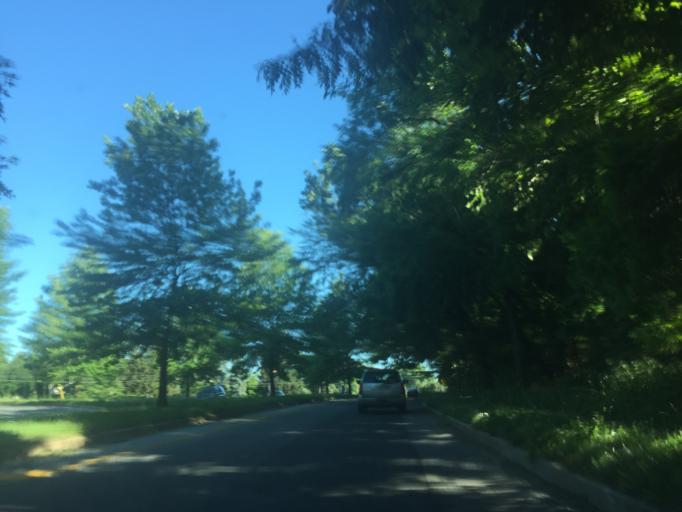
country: US
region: Maryland
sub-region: Baltimore County
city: Towson
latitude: 39.3831
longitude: -76.5792
